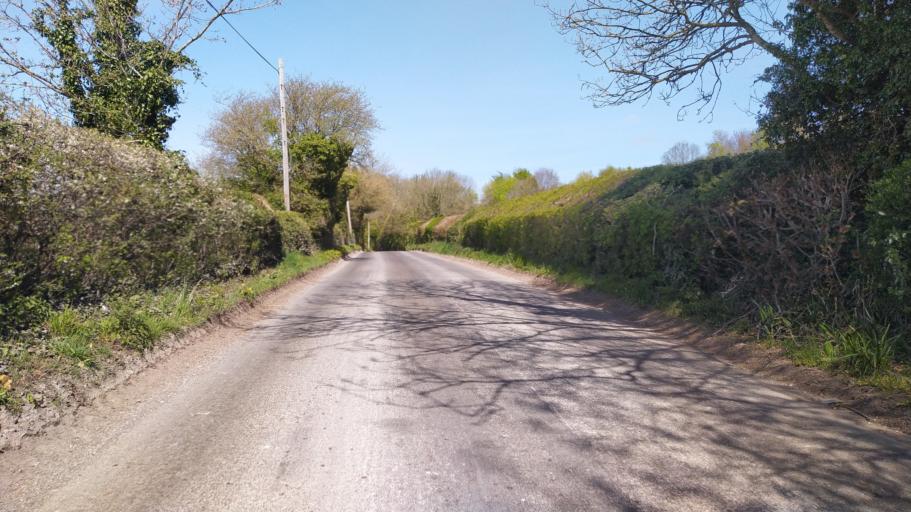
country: GB
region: England
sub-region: Dorset
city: Manston
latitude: 50.9021
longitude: -2.2213
